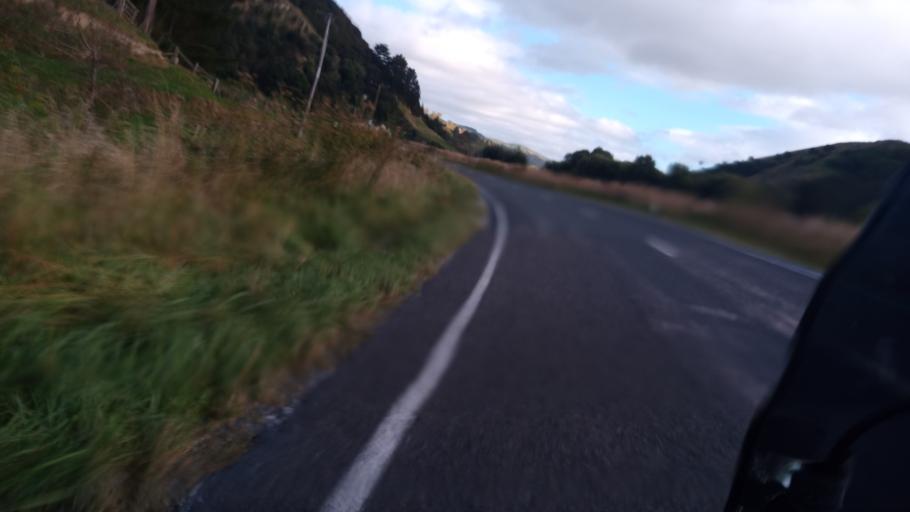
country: NZ
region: Gisborne
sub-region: Gisborne District
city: Gisborne
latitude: -38.6090
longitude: 177.8140
